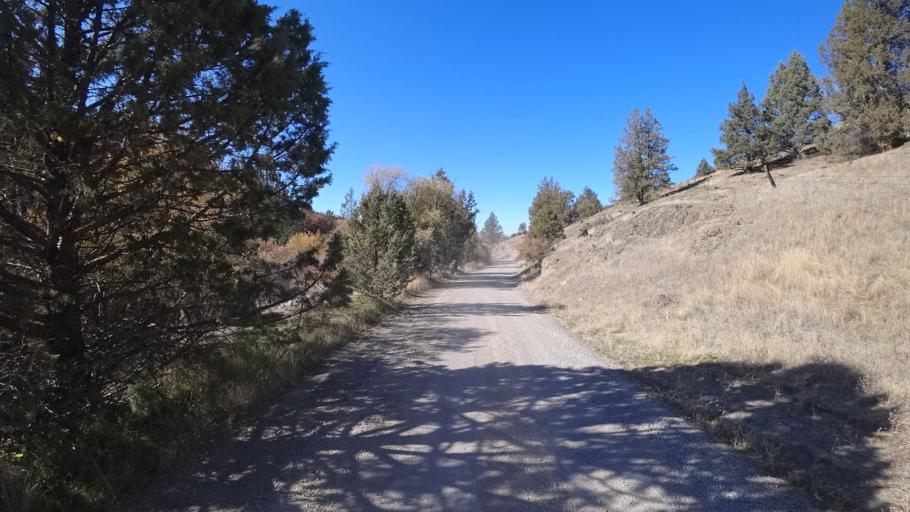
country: US
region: California
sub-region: Siskiyou County
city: Montague
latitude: 41.7927
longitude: -122.3558
